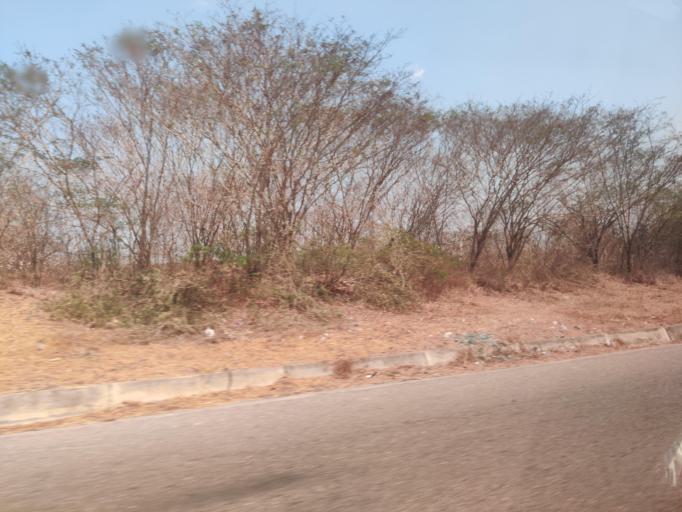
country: CO
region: Bolivar
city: Turbana
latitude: 10.2760
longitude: -75.5242
